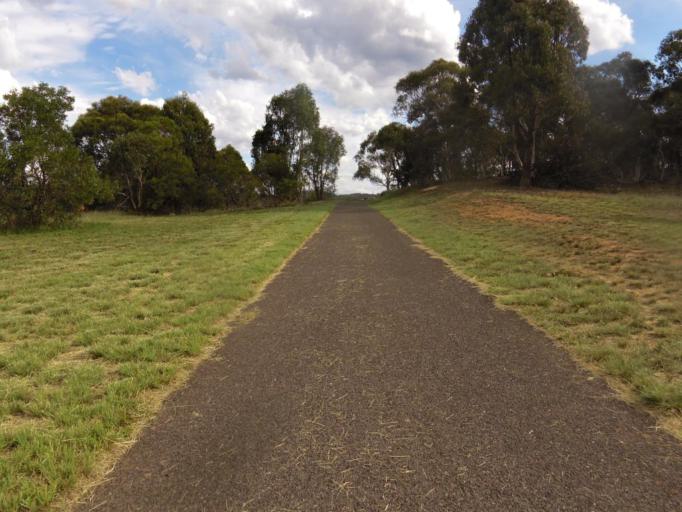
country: AU
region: Australian Capital Territory
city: Belconnen
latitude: -35.2223
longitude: 149.0809
